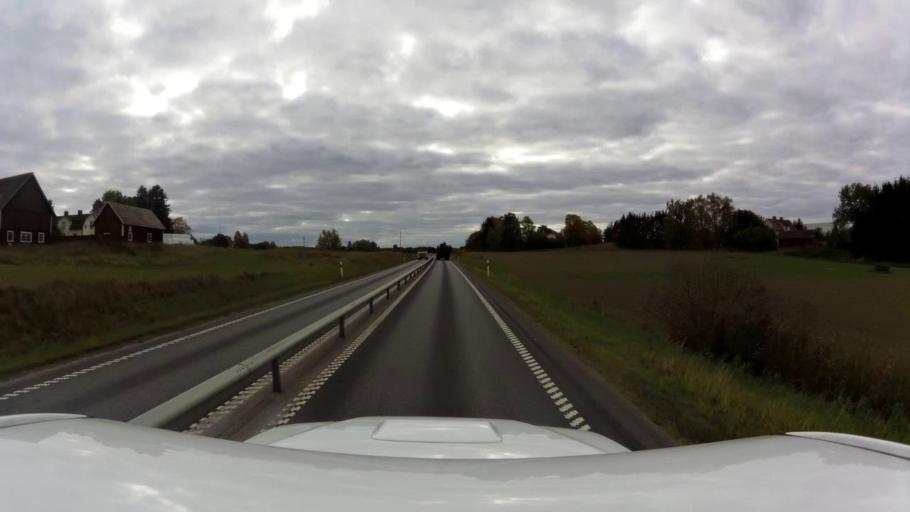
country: SE
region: OEstergoetland
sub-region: Linkopings Kommun
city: Malmslatt
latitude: 58.3365
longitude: 15.5572
